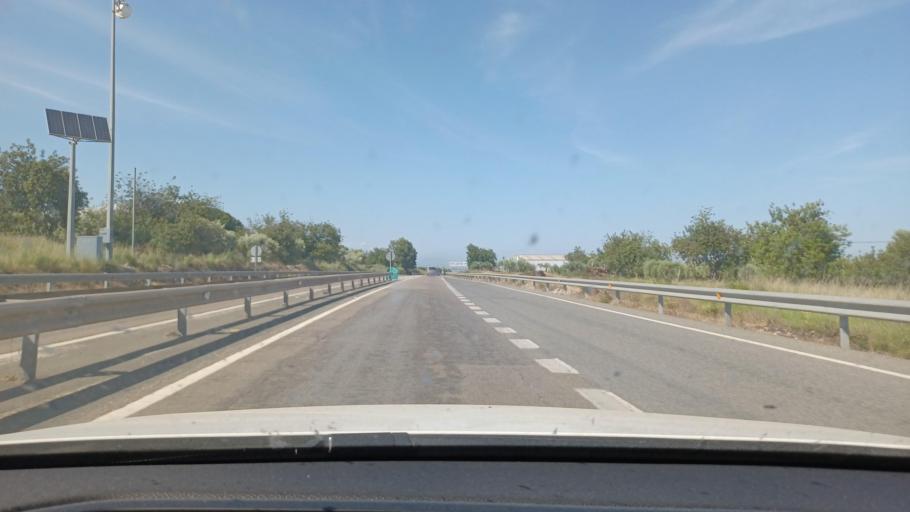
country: ES
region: Catalonia
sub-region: Provincia de Tarragona
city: Sant Carles de la Rapita
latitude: 40.6274
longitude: 0.5798
